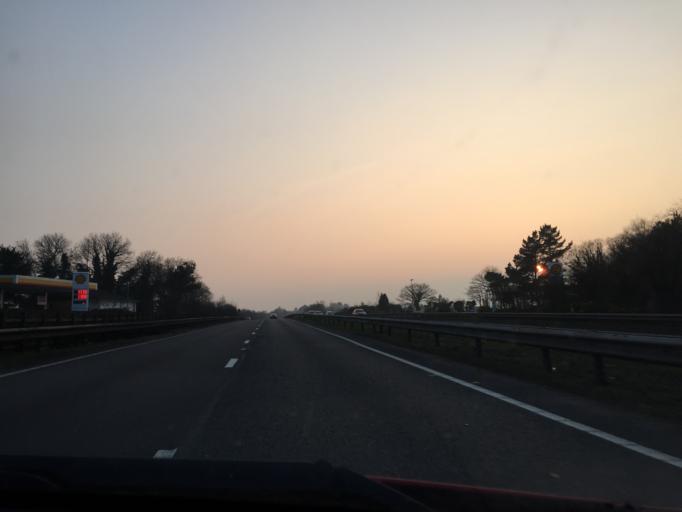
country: GB
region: England
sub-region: Hampshire
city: Ringwood
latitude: 50.8546
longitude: -1.7290
